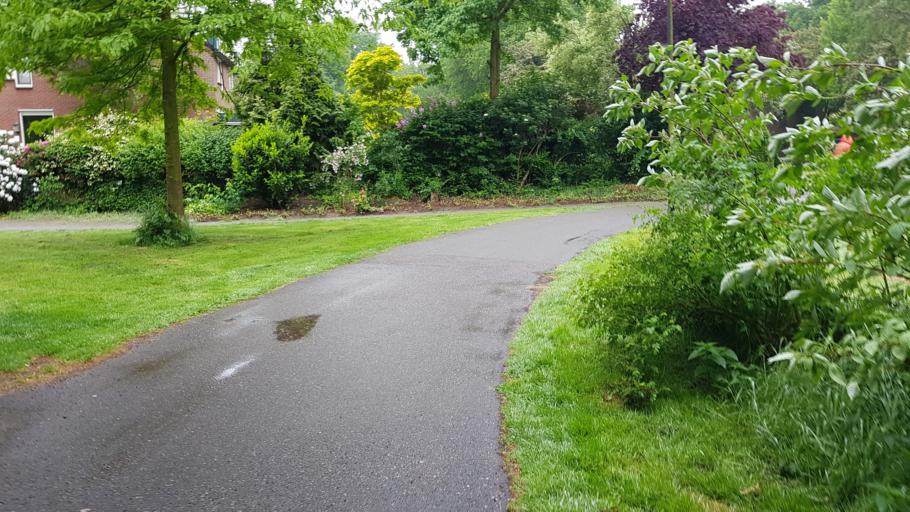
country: NL
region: Gelderland
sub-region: Gemeente Apeldoorn
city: Apeldoorn
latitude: 52.1897
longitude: 5.9982
